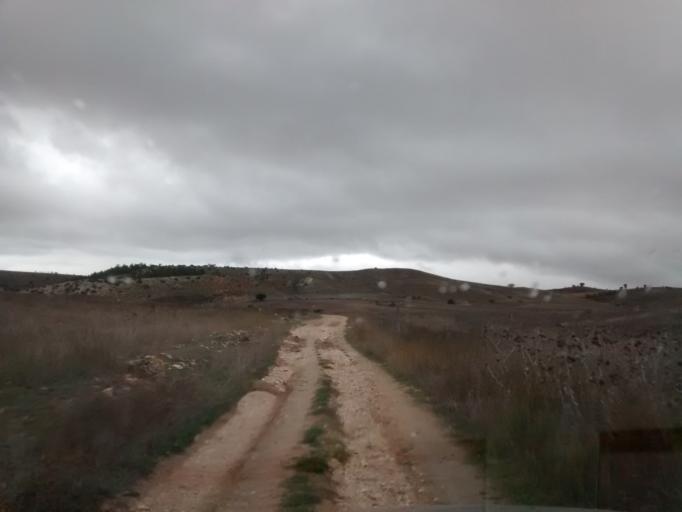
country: ES
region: Aragon
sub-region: Provincia de Zaragoza
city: Torralba de los Frailes
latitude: 41.0284
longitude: -1.6823
